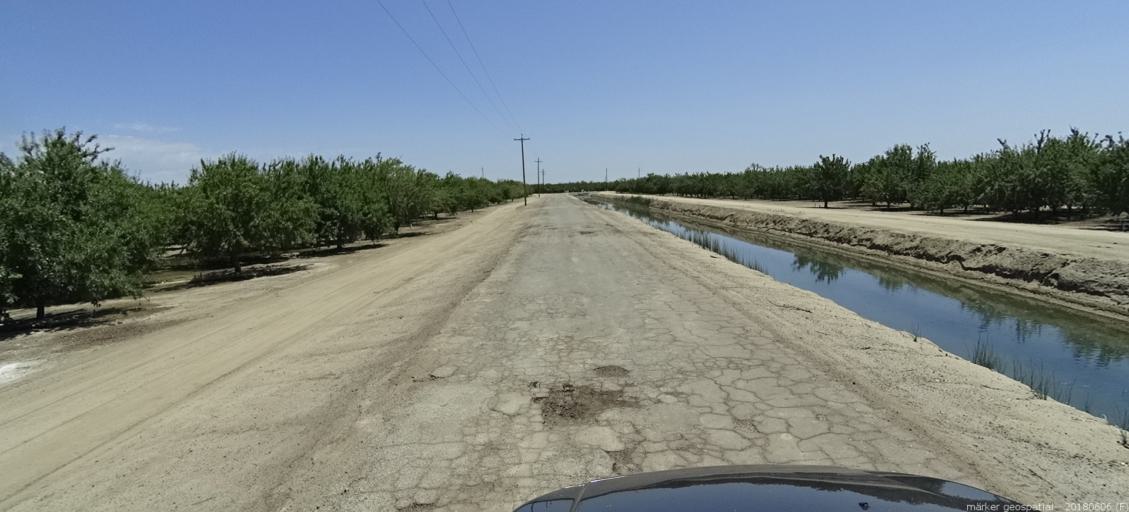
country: US
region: California
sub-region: Fresno County
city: Mendota
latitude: 36.7882
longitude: -120.3129
